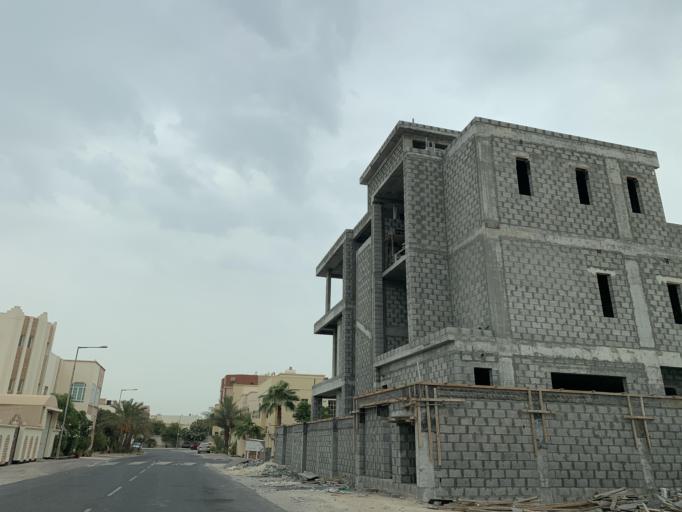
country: BH
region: Northern
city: Madinat `Isa
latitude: 26.1877
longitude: 50.4781
